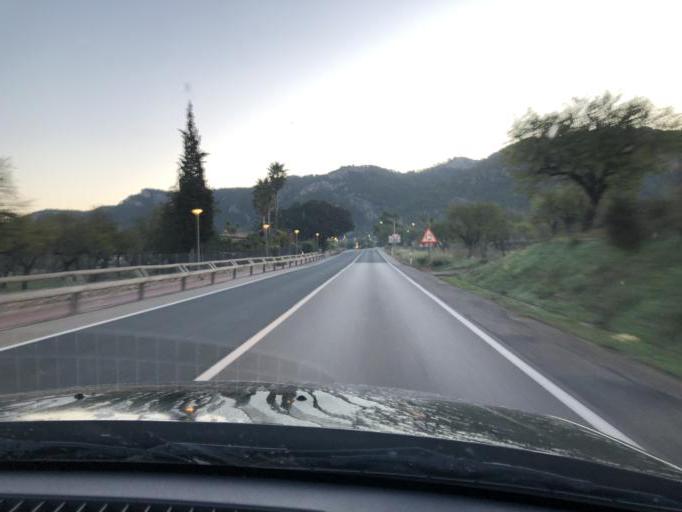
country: ES
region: Balearic Islands
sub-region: Illes Balears
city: Andratx
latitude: 39.5660
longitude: 2.4140
